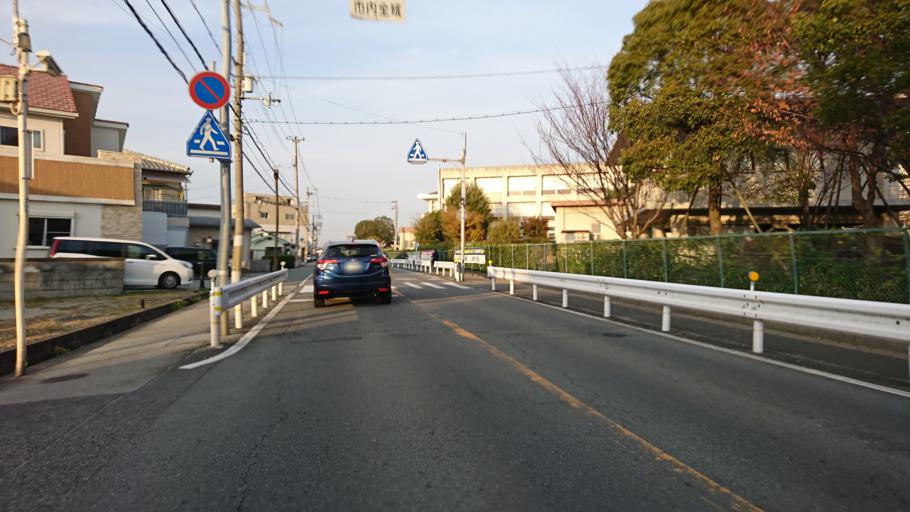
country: JP
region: Hyogo
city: Kakogawacho-honmachi
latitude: 34.7532
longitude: 134.8732
